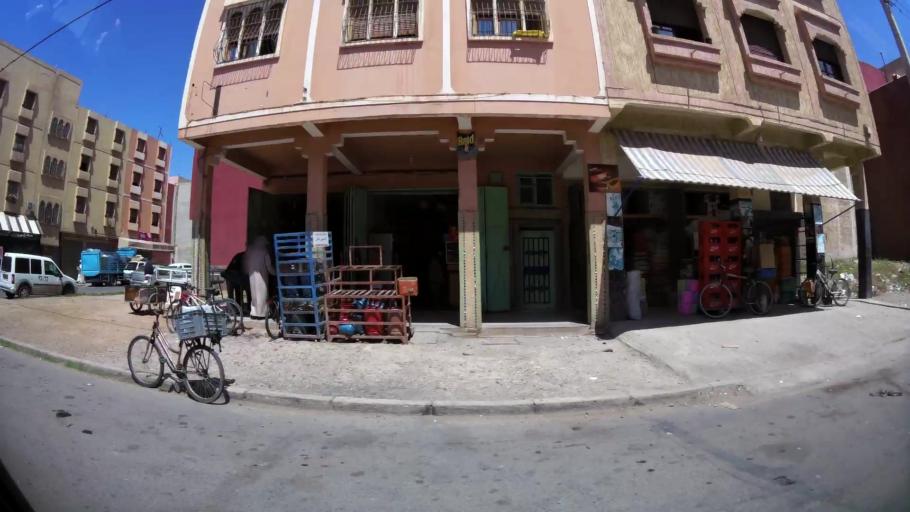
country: MA
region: Souss-Massa-Draa
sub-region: Inezgane-Ait Mellou
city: Inezgane
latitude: 30.3382
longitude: -9.5018
